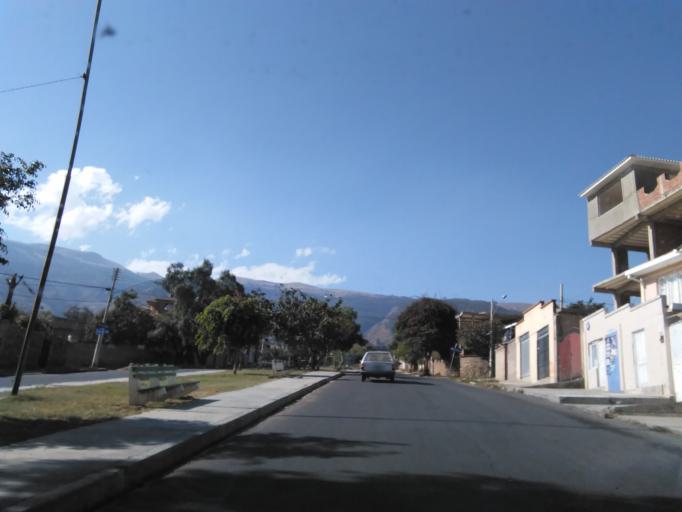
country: BO
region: Cochabamba
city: Cochabamba
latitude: -17.3537
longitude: -66.1645
